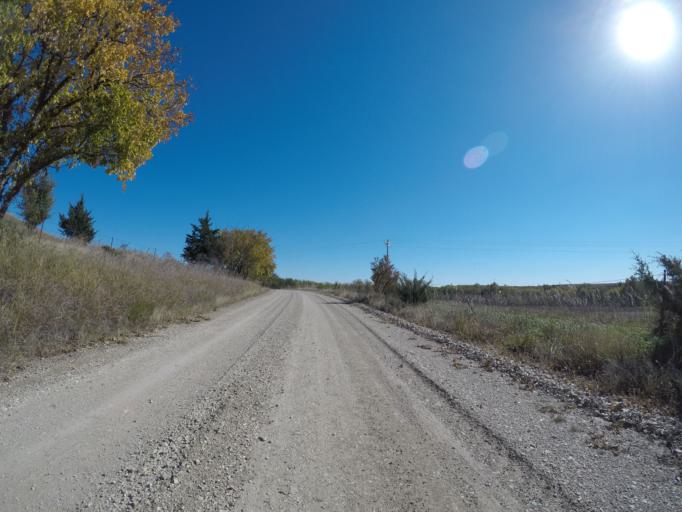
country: US
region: Kansas
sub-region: Wabaunsee County
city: Alma
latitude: 38.9829
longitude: -96.4616
